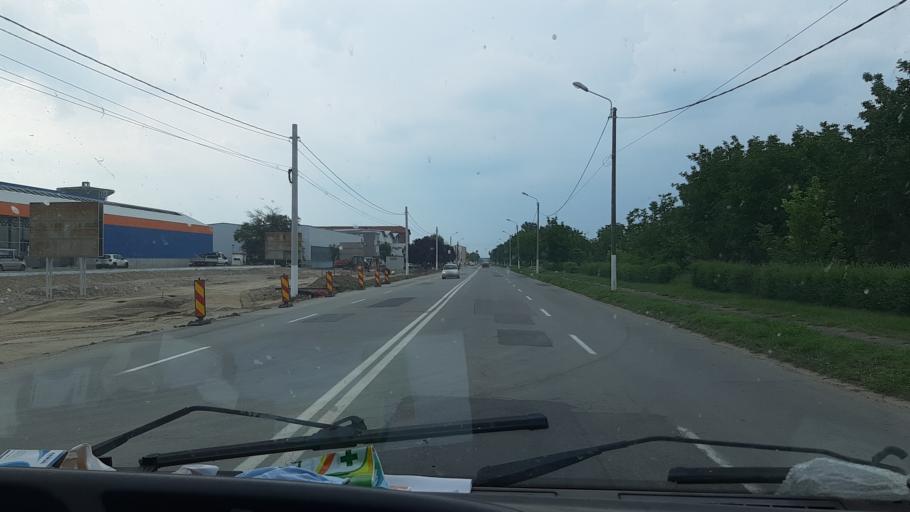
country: RO
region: Timis
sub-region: Municipiul Lugoj
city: Lugoj
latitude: 45.7035
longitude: 21.8915
